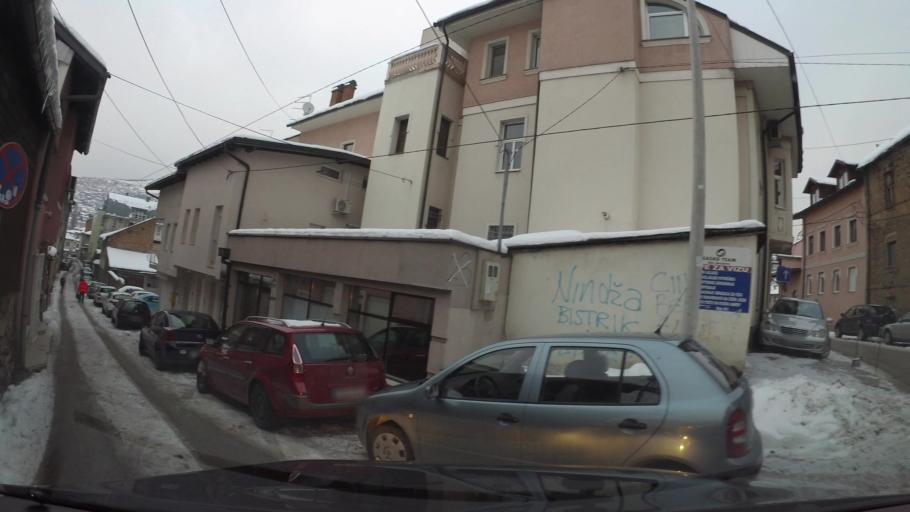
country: BA
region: Federation of Bosnia and Herzegovina
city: Kobilja Glava
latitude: 43.8560
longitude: 18.4337
